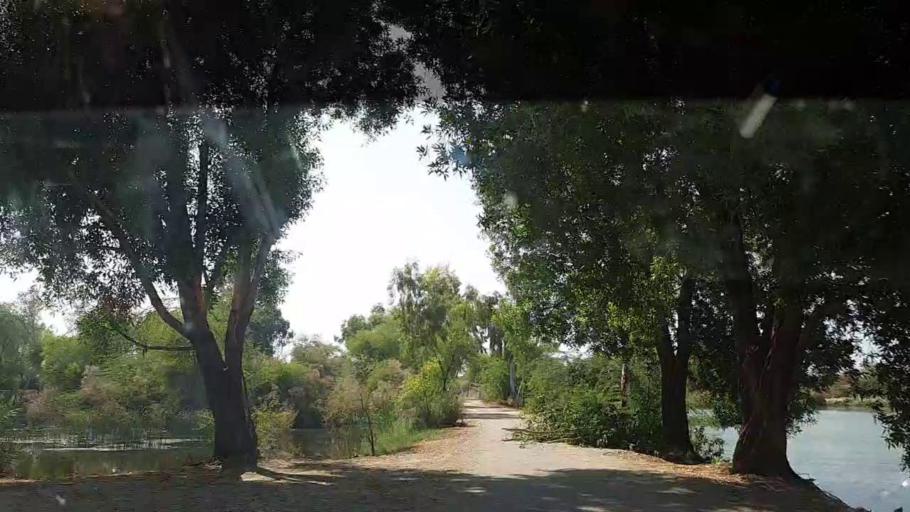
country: PK
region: Sindh
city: Ghauspur
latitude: 28.2186
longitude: 69.0928
